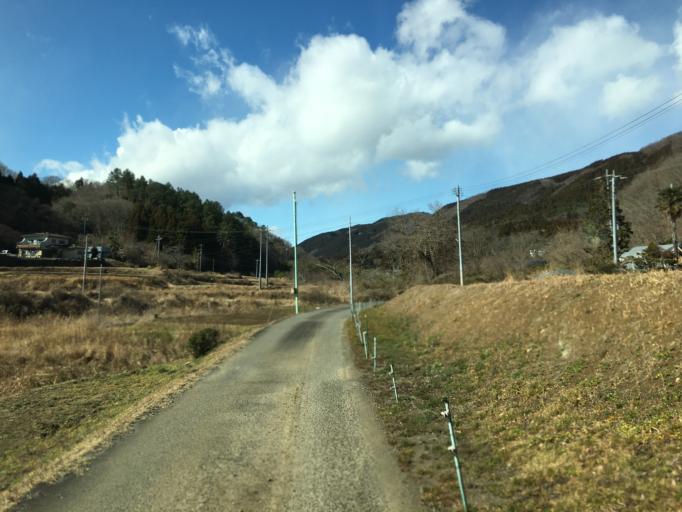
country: JP
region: Fukushima
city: Iwaki
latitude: 37.0062
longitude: 140.7959
